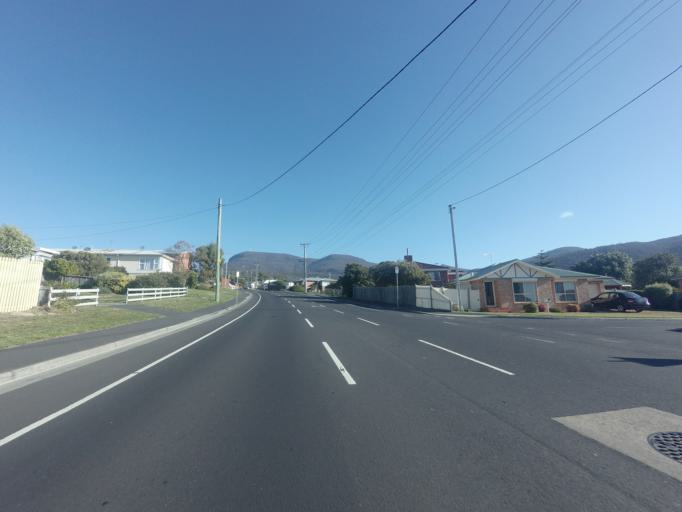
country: AU
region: Tasmania
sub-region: Glenorchy
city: Glenorchy
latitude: -42.8445
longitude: 147.2659
